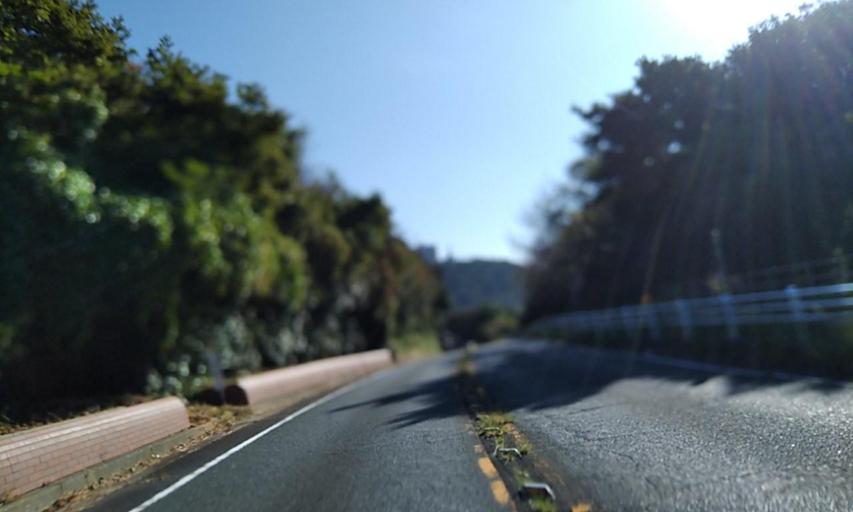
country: JP
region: Aichi
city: Toyohama
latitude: 34.5822
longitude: 137.0286
